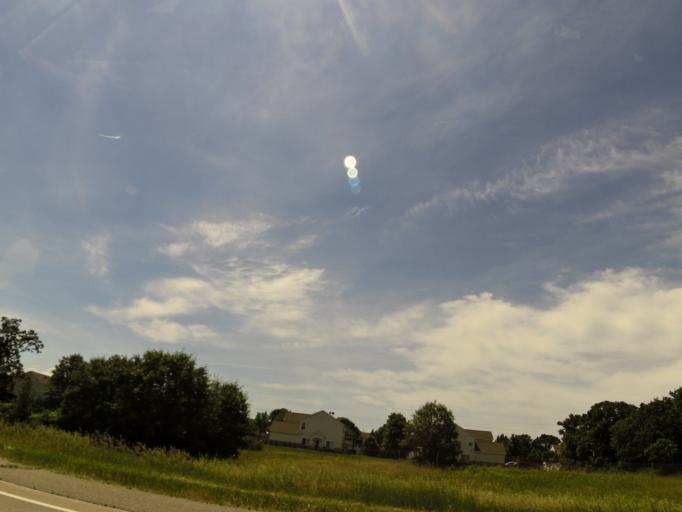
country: US
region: Minnesota
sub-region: Scott County
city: Prior Lake
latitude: 44.7829
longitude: -93.4215
